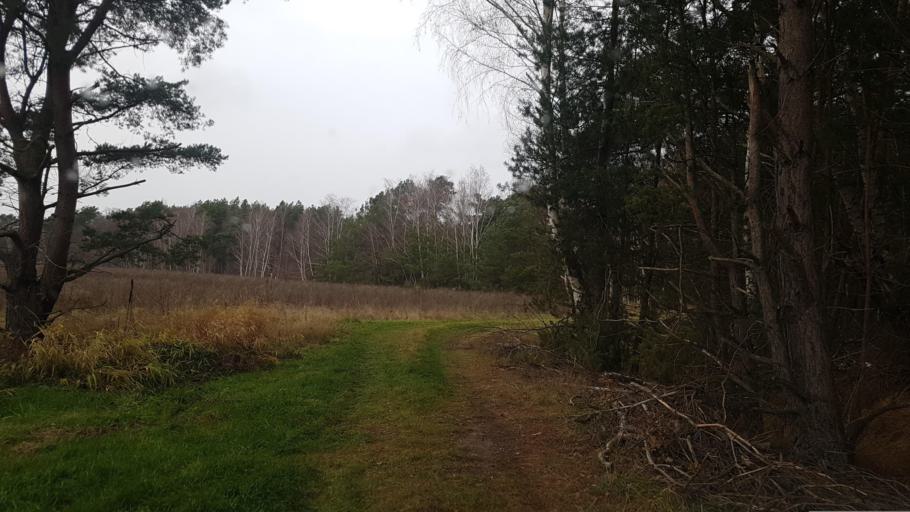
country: DE
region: Brandenburg
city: Ruckersdorf
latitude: 51.5628
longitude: 13.6018
